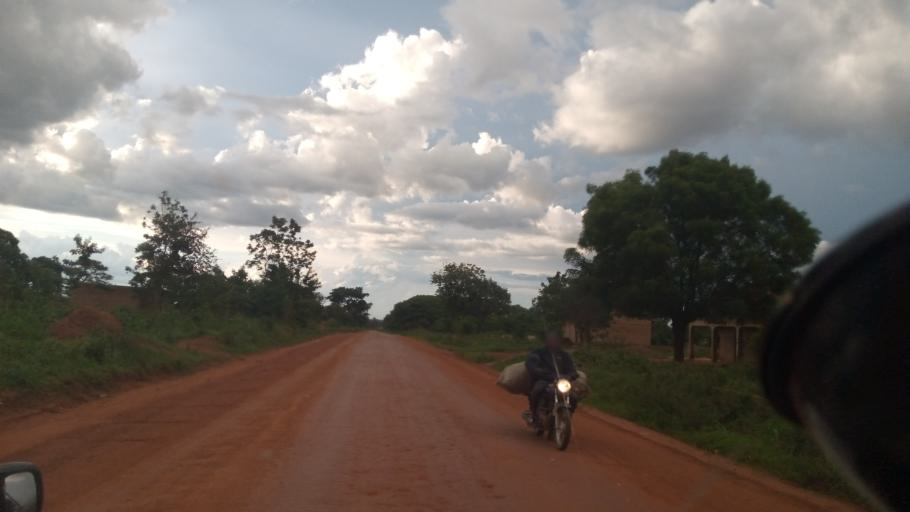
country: UG
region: Northern Region
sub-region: Lira District
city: Lira
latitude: 2.3724
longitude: 32.9352
